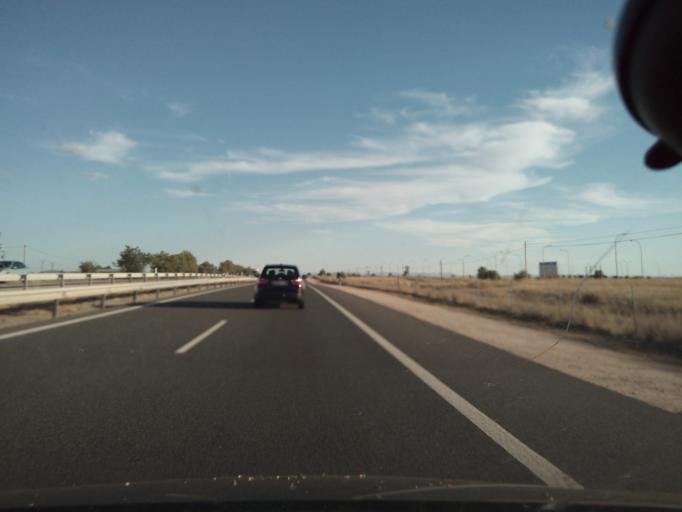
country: ES
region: Castille-La Mancha
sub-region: Province of Toledo
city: Tembleque
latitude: 39.7715
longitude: -3.4798
